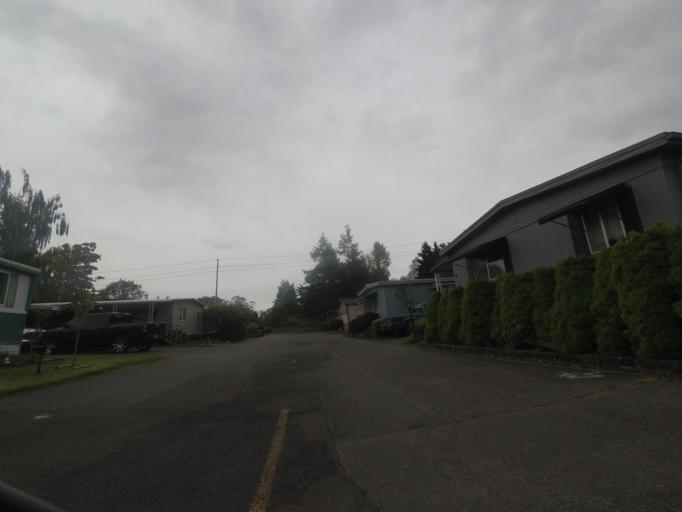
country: US
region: Washington
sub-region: Pierce County
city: Lakewood
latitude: 47.1841
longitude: -122.4790
